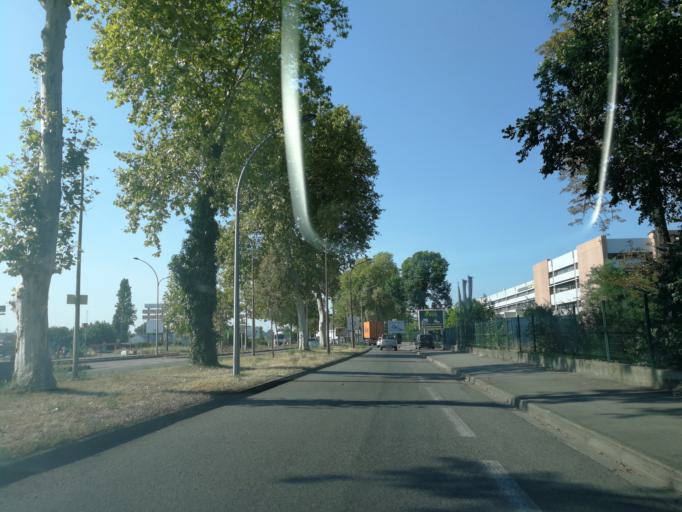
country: FR
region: Midi-Pyrenees
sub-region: Departement de la Haute-Garonne
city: Aucamville
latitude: 43.6437
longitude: 1.4281
